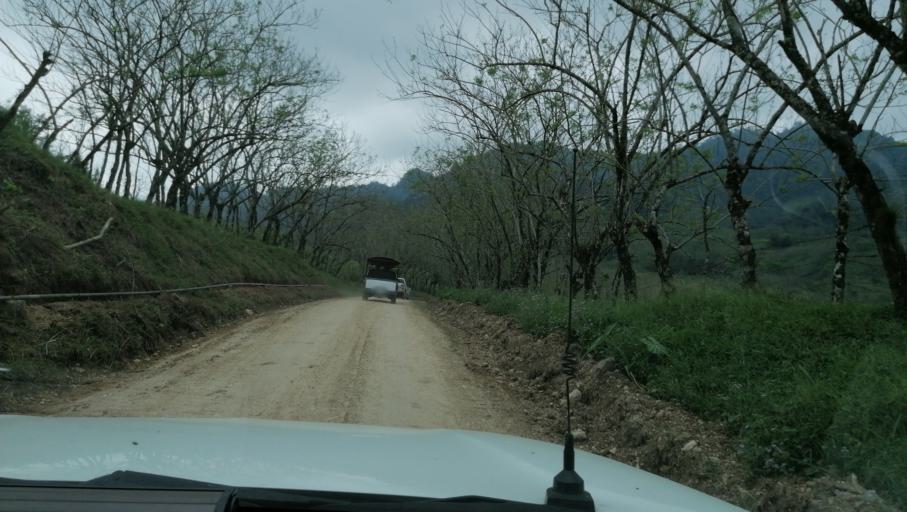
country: MX
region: Chiapas
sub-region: Ocotepec
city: San Pablo Huacano
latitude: 17.2690
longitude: -93.2593
